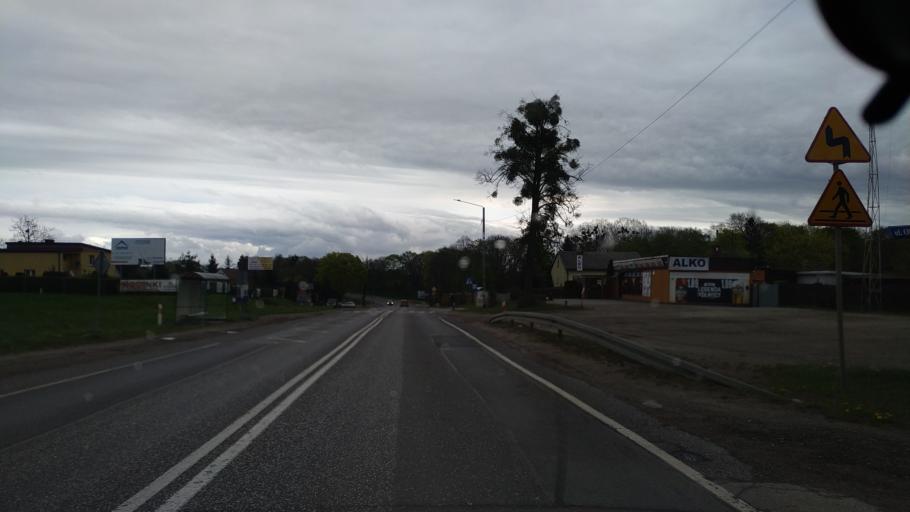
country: PL
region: Pomeranian Voivodeship
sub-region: Powiat starogardzki
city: Starogard Gdanski
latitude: 53.9453
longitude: 18.4644
